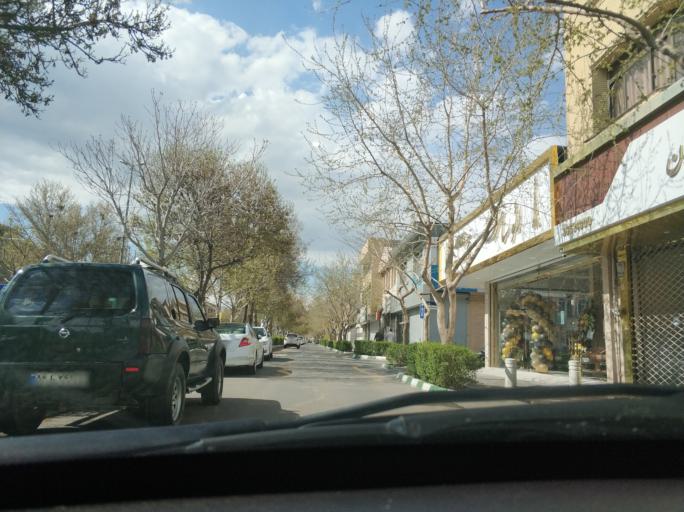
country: IR
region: Razavi Khorasan
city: Mashhad
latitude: 36.2719
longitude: 59.5951
